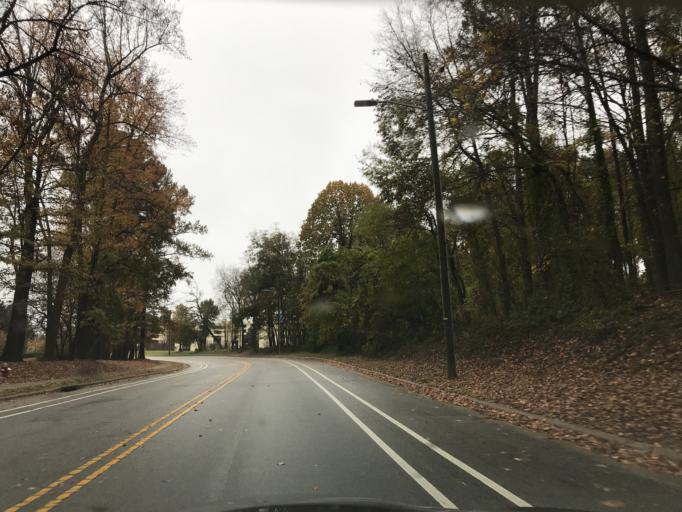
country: US
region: North Carolina
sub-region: Wake County
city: West Raleigh
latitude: 35.8324
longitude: -78.6228
